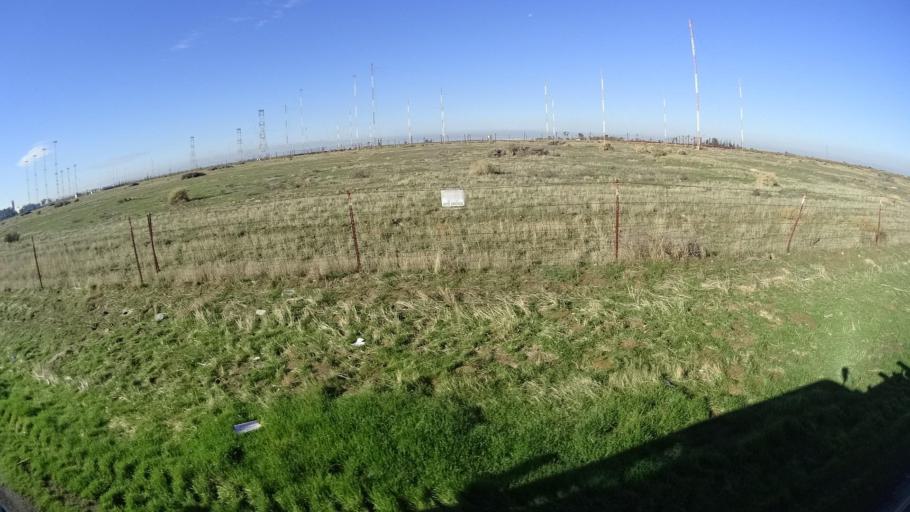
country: US
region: California
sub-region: Kern County
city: Delano
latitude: 35.7590
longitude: -119.2763
